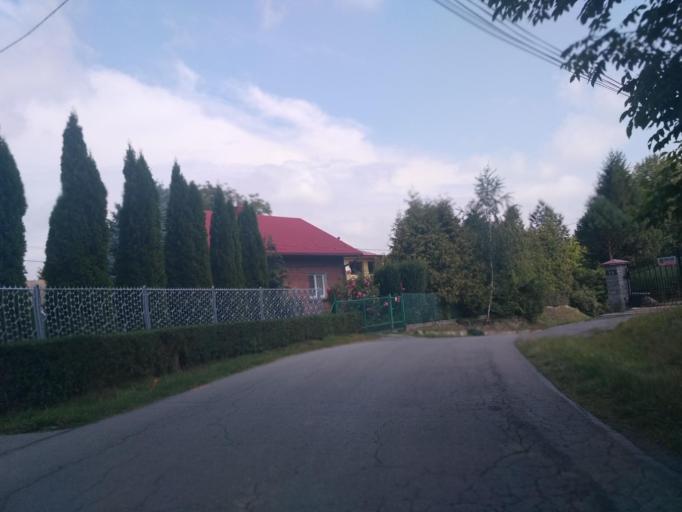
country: PL
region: Subcarpathian Voivodeship
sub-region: Powiat lancucki
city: Kraczkowa
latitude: 50.0363
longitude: 22.1713
